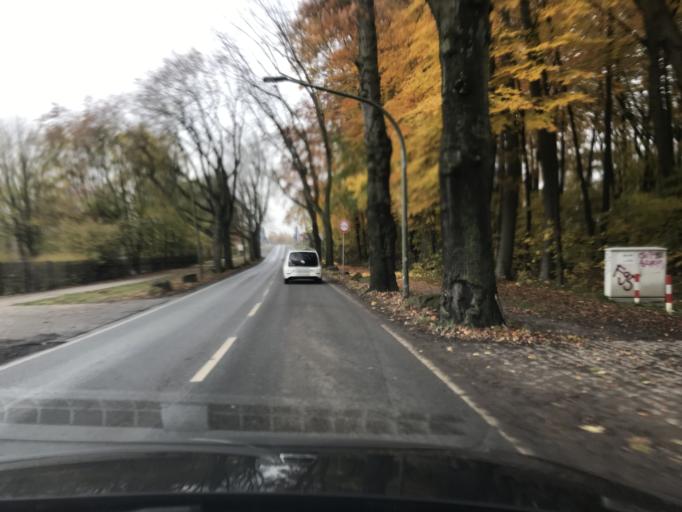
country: DE
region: North Rhine-Westphalia
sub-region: Regierungsbezirk Arnsberg
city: Hamm
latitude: 51.6914
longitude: 7.8414
